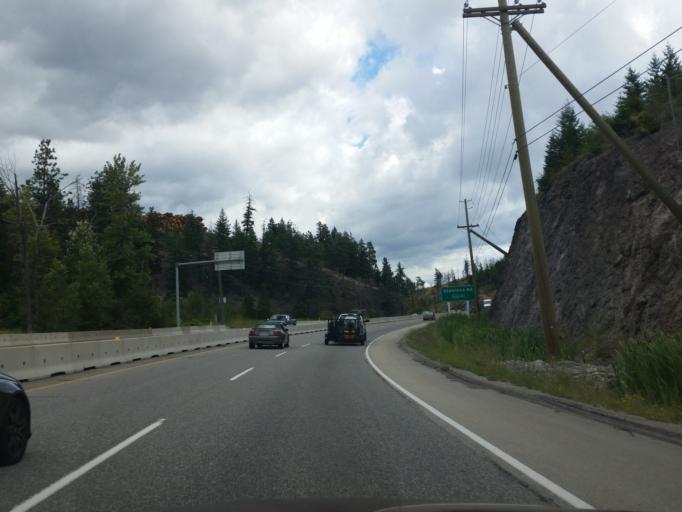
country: CA
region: British Columbia
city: West Kelowna
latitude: 49.8135
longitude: -119.6575
